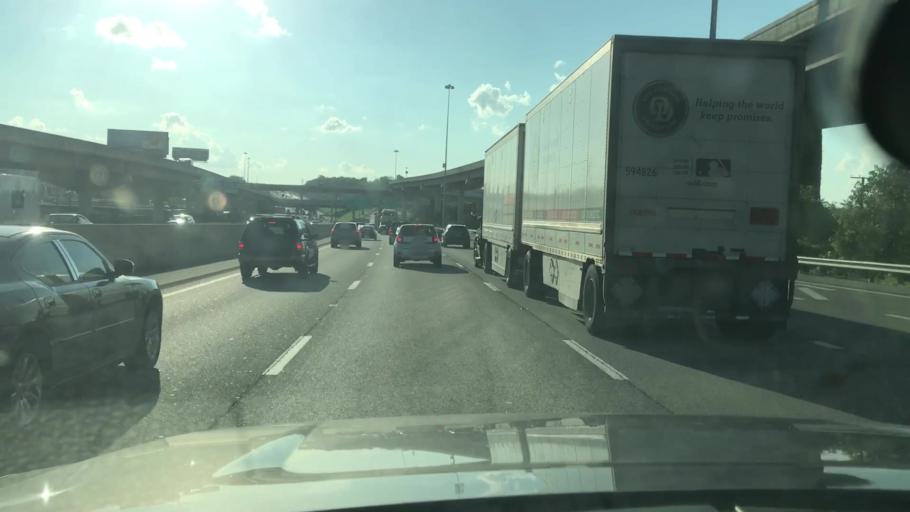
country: US
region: Tennessee
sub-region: Davidson County
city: Belle Meade
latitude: 36.1496
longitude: -86.8490
